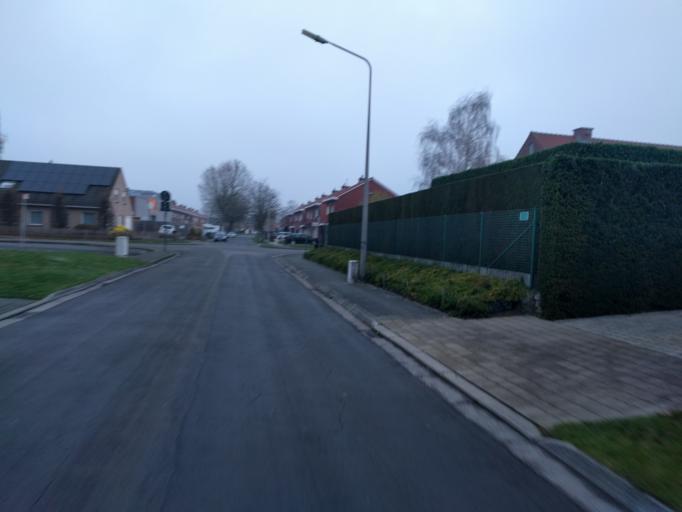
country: BE
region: Flanders
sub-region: Provincie West-Vlaanderen
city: Kortrijk
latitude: 50.8284
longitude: 3.2277
